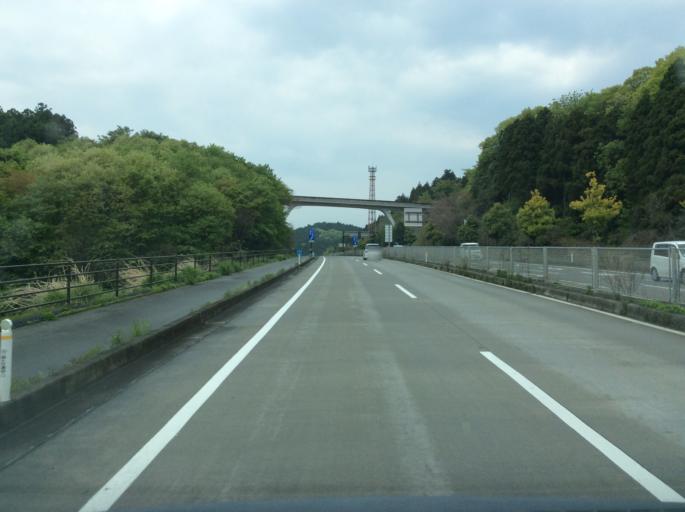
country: JP
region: Fukushima
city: Iwaki
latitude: 37.0214
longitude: 140.8905
